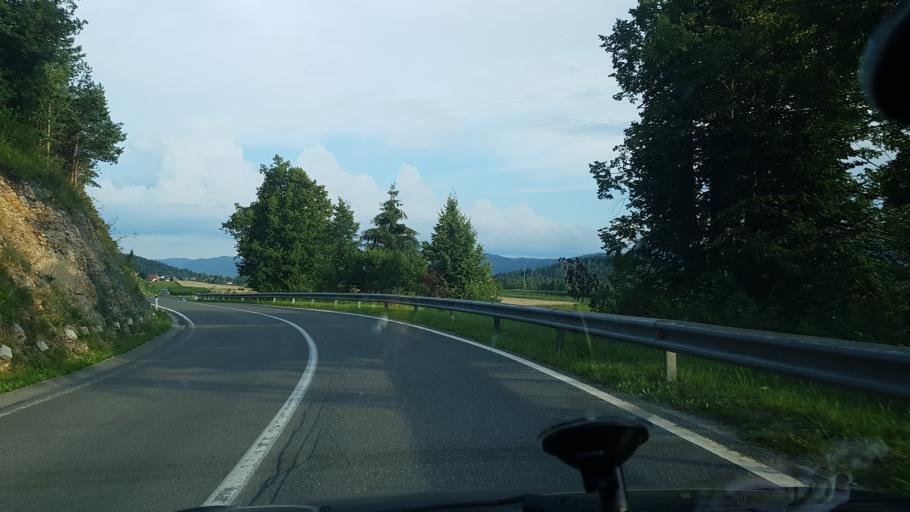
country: SI
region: Logatec
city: Logatec
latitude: 45.9379
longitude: 14.1281
